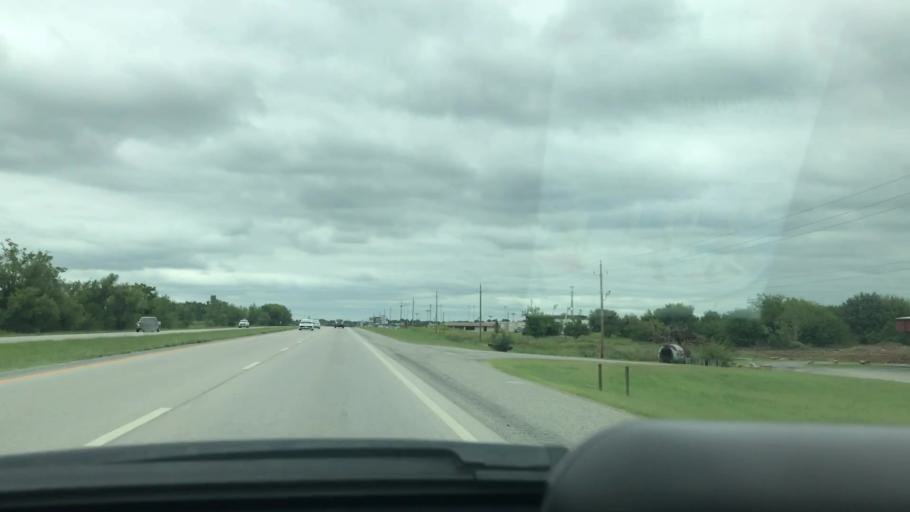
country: US
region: Oklahoma
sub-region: Mayes County
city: Pryor
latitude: 36.2554
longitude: -95.3346
